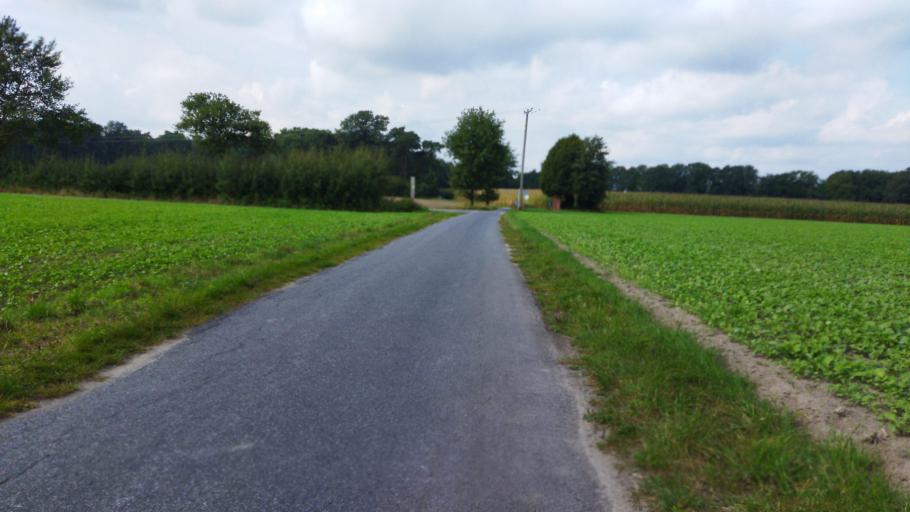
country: DE
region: North Rhine-Westphalia
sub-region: Regierungsbezirk Munster
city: Everswinkel
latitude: 51.9637
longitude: 7.9093
